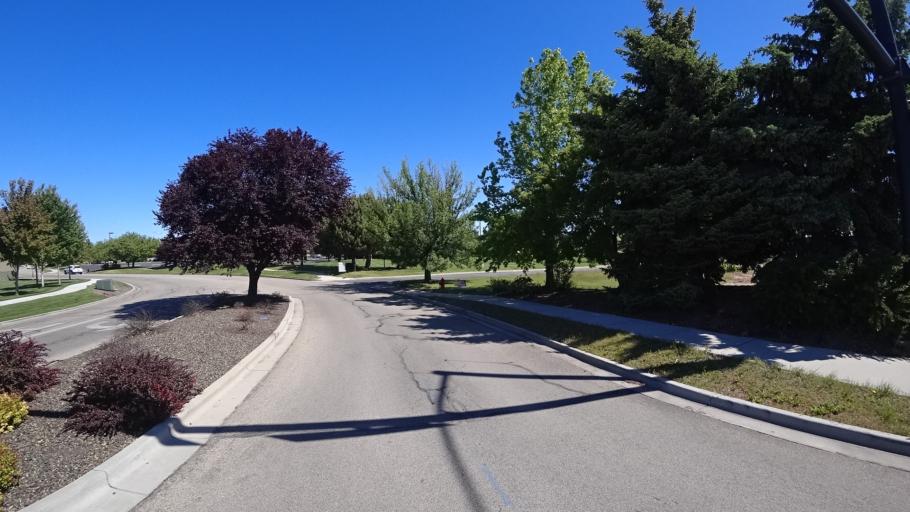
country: US
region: Idaho
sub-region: Ada County
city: Meridian
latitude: 43.6197
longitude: -116.3610
